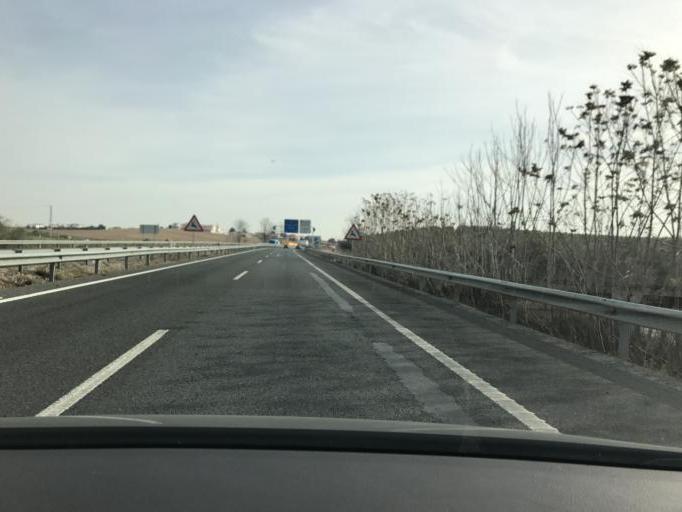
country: ES
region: Andalusia
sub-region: Provincia de Granada
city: Moraleda de Zafayona
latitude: 37.1876
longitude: -3.9653
